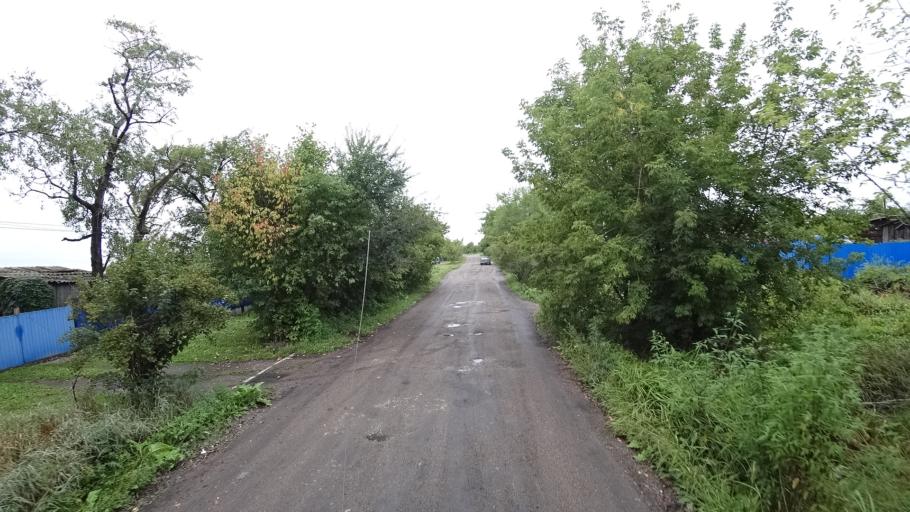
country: RU
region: Primorskiy
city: Monastyrishche
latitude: 44.1973
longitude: 132.4647
